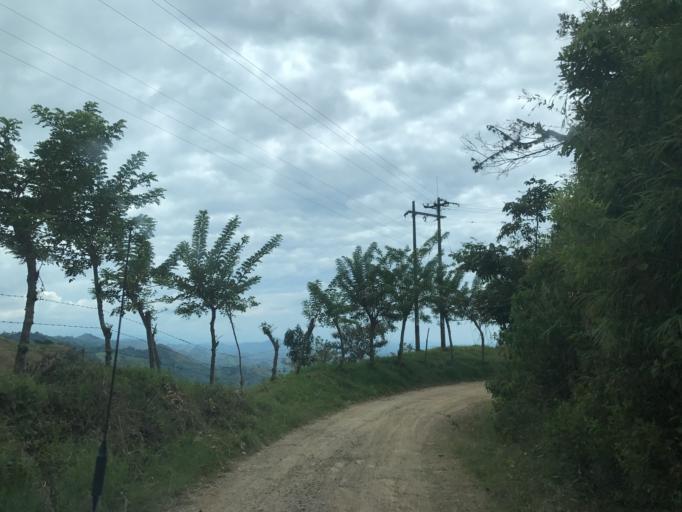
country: CO
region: Valle del Cauca
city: Obando
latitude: 4.5484
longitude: -75.9222
